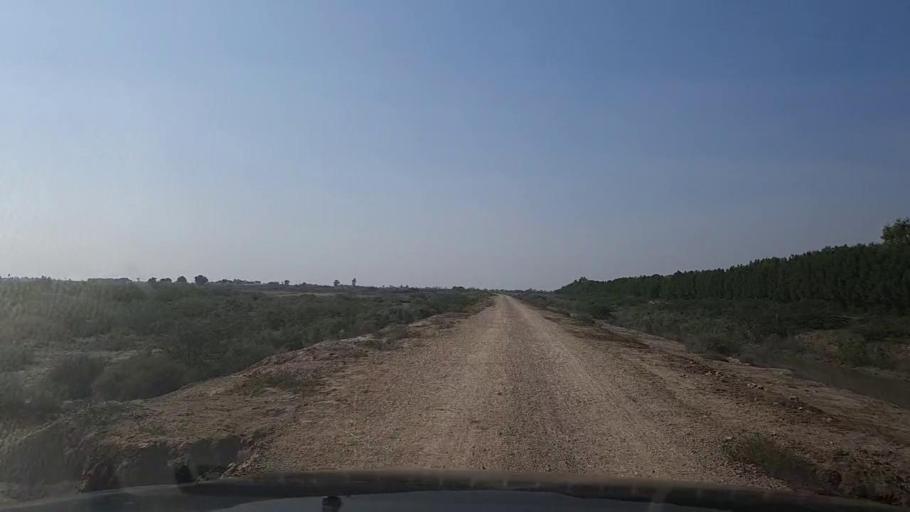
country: PK
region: Sindh
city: Thatta
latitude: 24.7111
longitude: 67.7579
